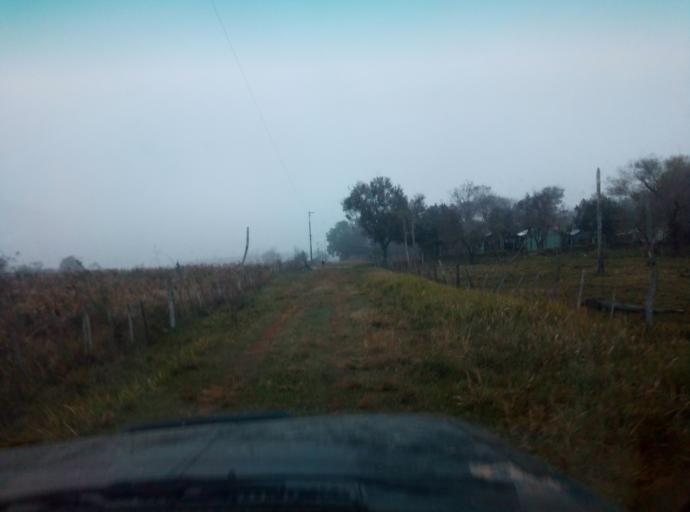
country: PY
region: Caaguazu
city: Doctor Cecilio Baez
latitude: -25.1568
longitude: -56.2613
